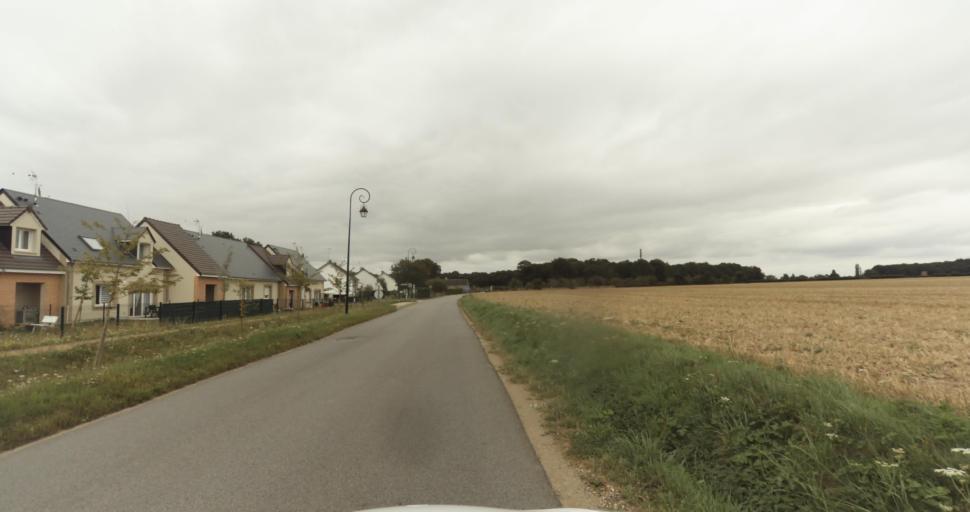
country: FR
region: Haute-Normandie
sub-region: Departement de l'Eure
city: Arnieres-sur-Iton
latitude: 48.9671
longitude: 1.1028
